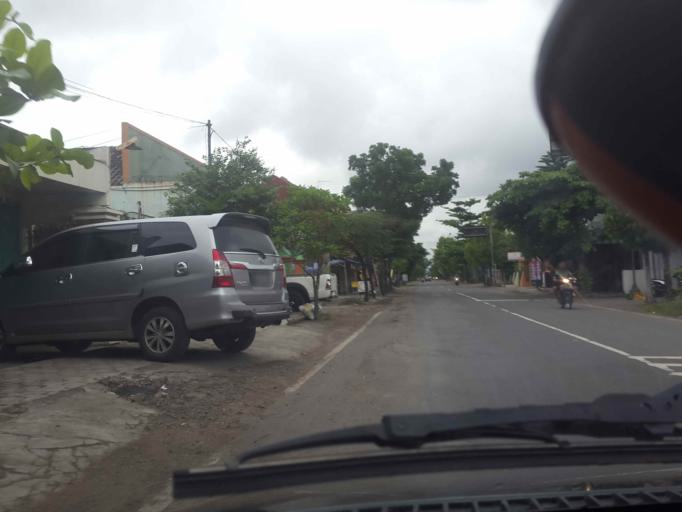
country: ID
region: Central Java
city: Sragen
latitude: -7.4269
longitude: 111.0329
